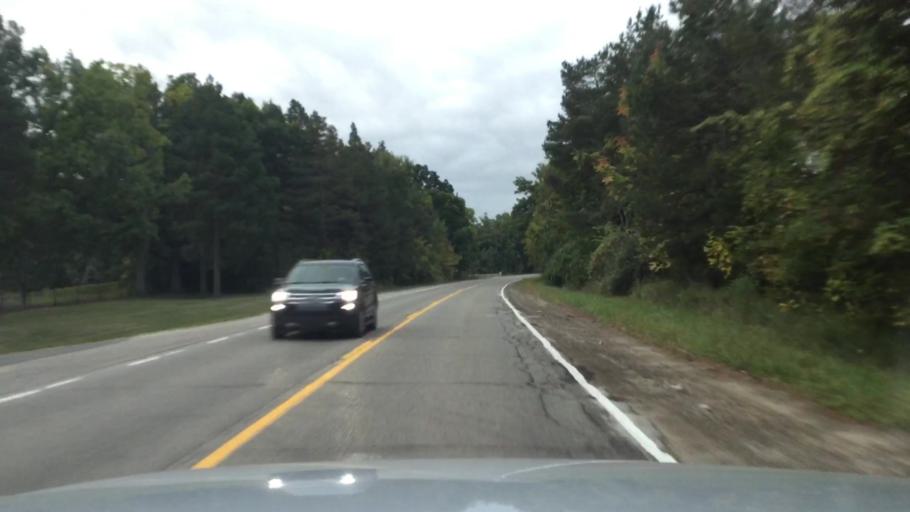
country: US
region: Michigan
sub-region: Livingston County
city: Brighton
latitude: 42.6133
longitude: -83.7481
